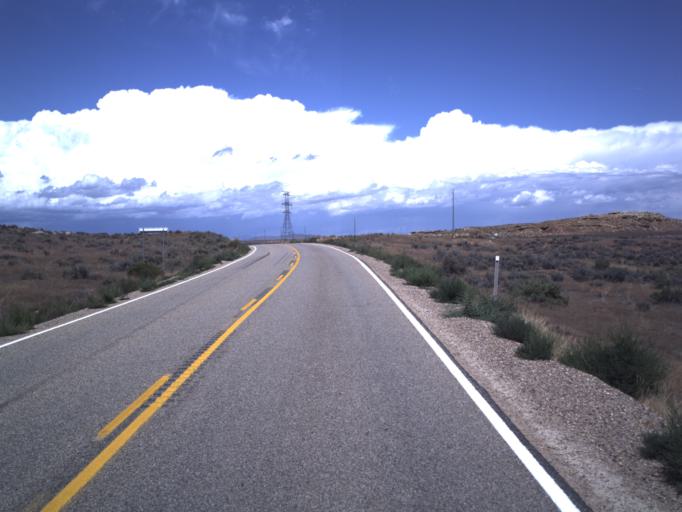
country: US
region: Utah
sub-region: Uintah County
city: Maeser
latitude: 40.2661
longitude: -109.6843
